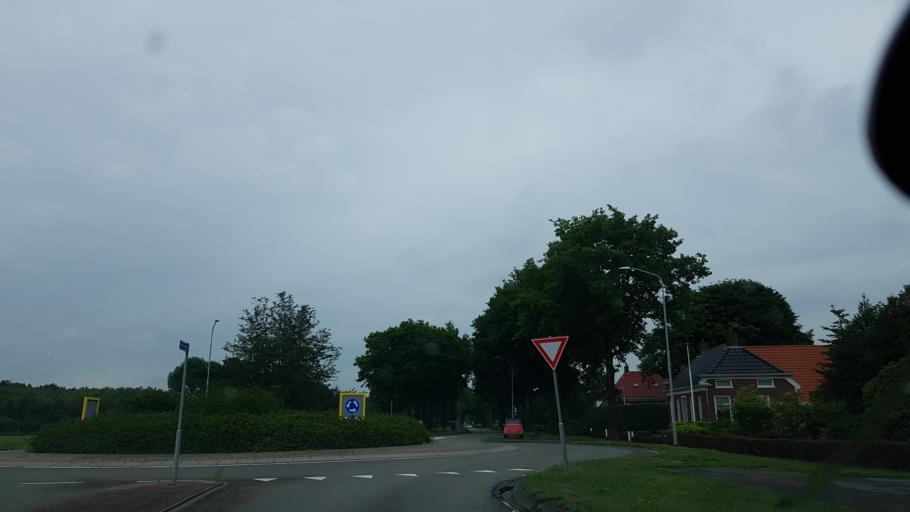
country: NL
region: Groningen
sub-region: Gemeente Hoogezand-Sappemeer
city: Hoogezand
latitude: 53.1416
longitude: 6.7239
